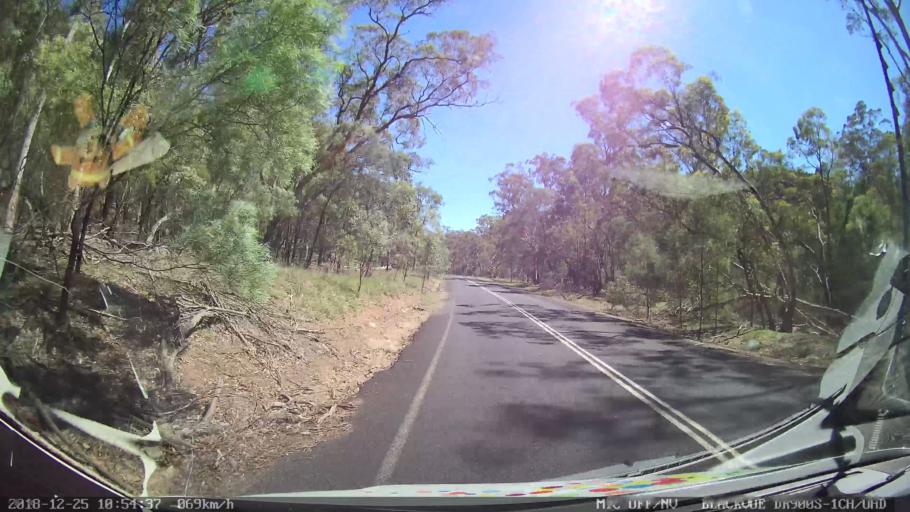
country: AU
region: New South Wales
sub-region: Upper Hunter Shire
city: Merriwa
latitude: -32.4079
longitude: 150.2735
